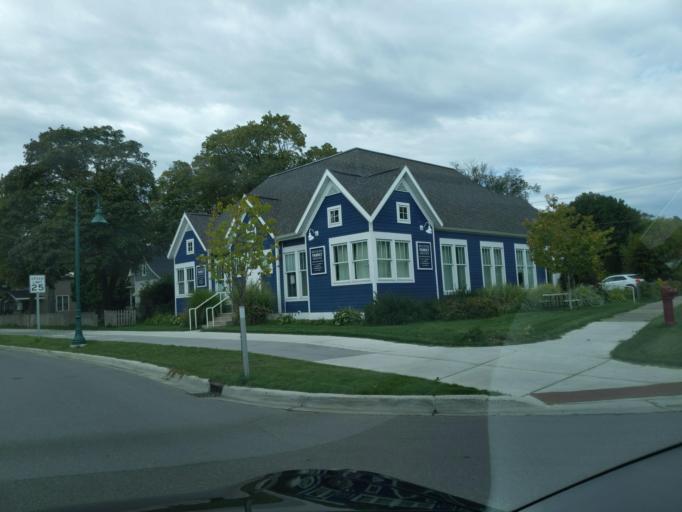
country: US
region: Michigan
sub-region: Grand Traverse County
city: Traverse City
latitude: 44.7594
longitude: -85.6085
